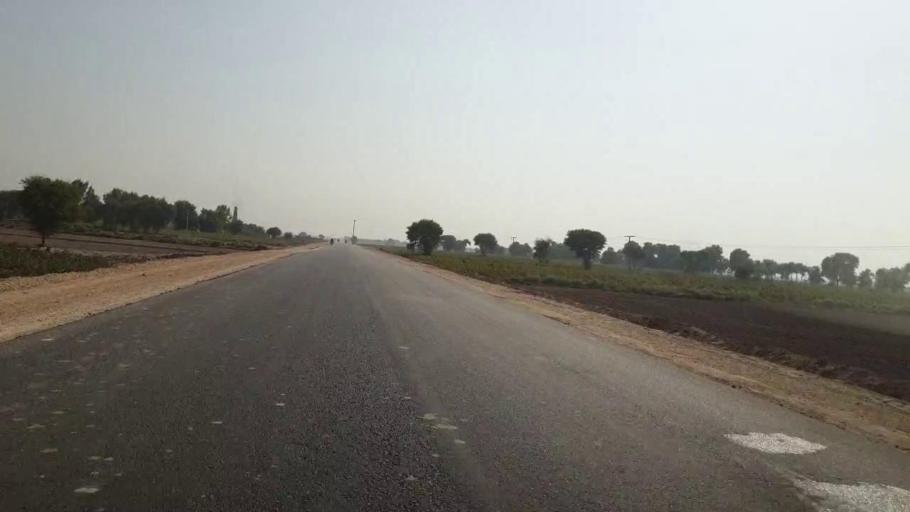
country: PK
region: Sindh
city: Dadu
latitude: 26.6635
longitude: 67.7764
